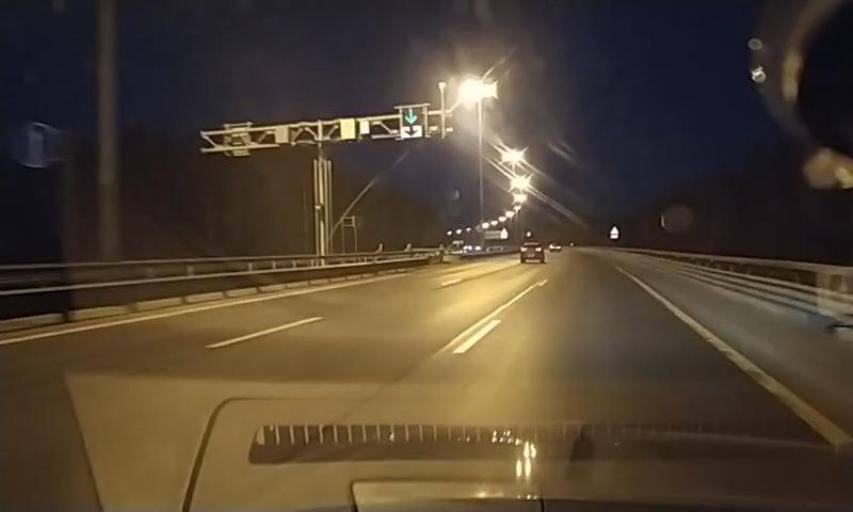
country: RU
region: St.-Petersburg
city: Pesochnyy
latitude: 60.0731
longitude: 30.1337
